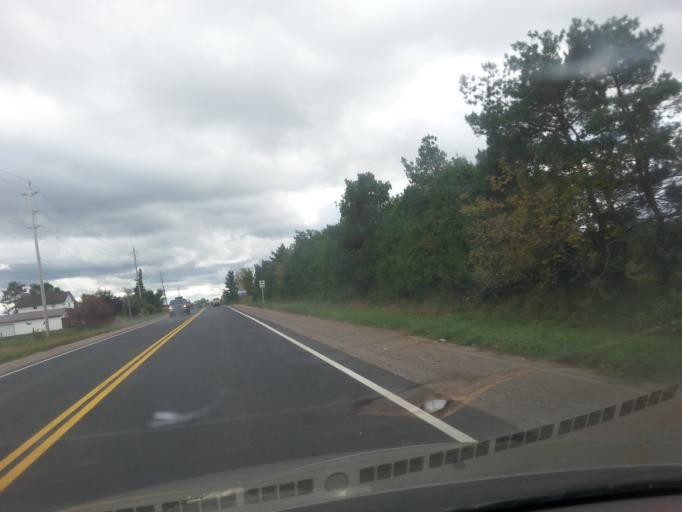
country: CA
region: Ontario
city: Pembroke
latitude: 45.5592
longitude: -77.1154
